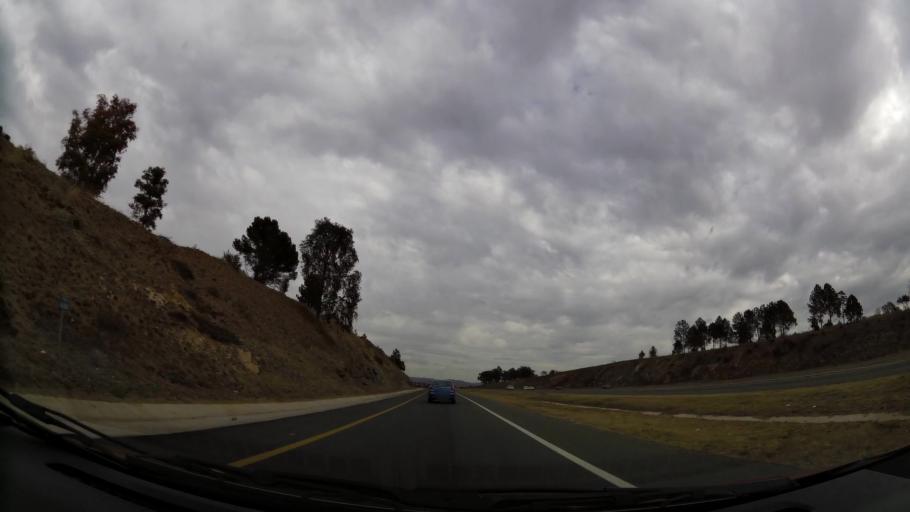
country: ZA
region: Gauteng
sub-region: West Rand District Municipality
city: Muldersdriseloop
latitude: -26.0212
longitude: 27.8581
